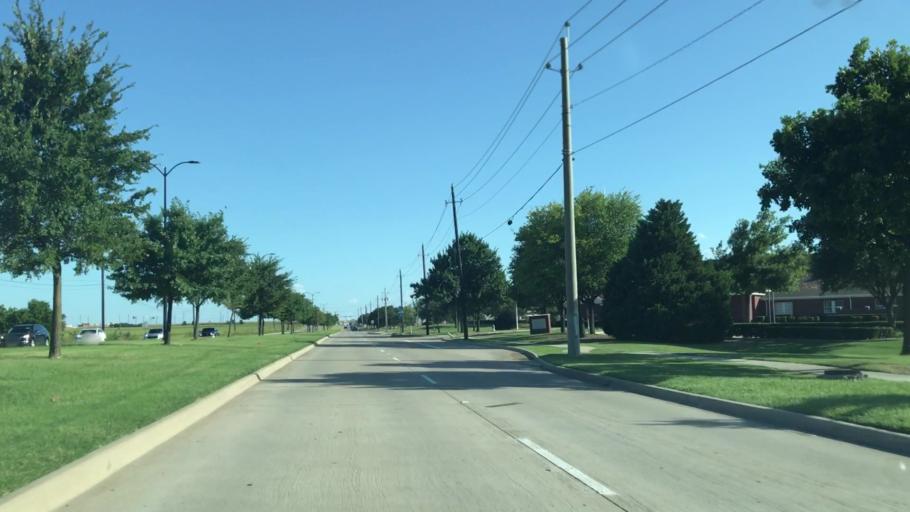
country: US
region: Texas
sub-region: Collin County
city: Frisco
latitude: 33.1214
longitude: -96.7681
